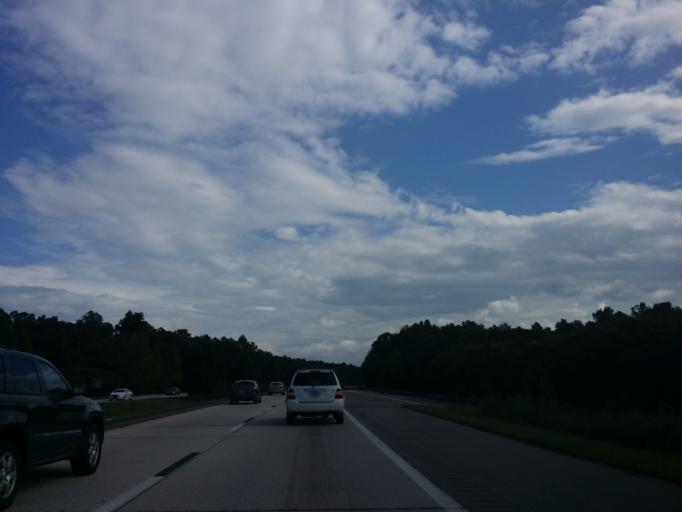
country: US
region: North Carolina
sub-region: Durham County
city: Durham
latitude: 35.9377
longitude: -78.8592
